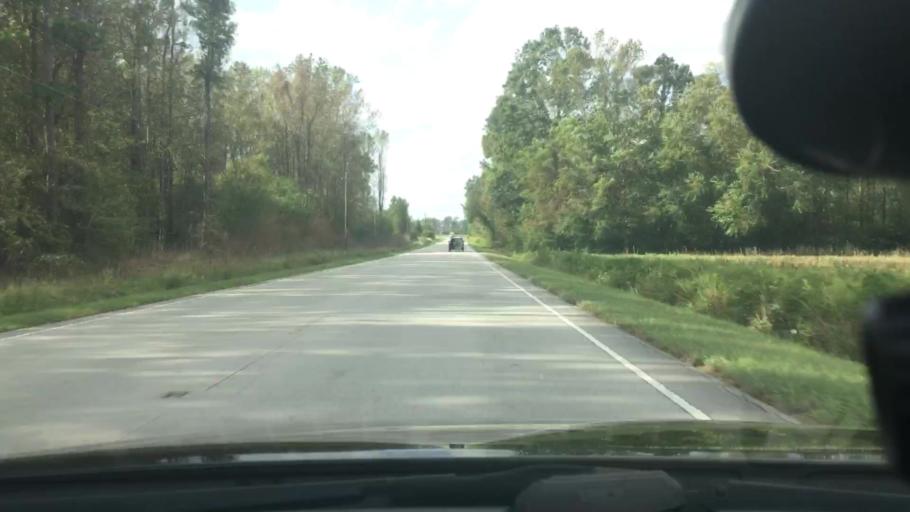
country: US
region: North Carolina
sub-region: Craven County
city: Vanceboro
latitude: 35.3678
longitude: -77.2041
